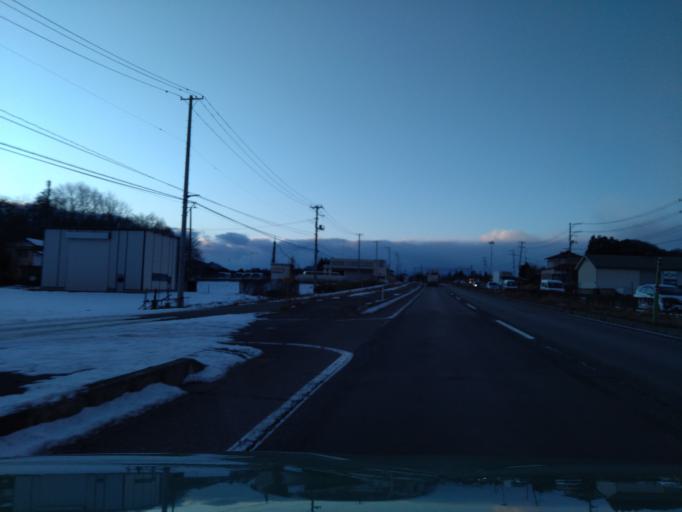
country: JP
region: Iwate
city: Shizukuishi
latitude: 39.7003
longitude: 141.0524
